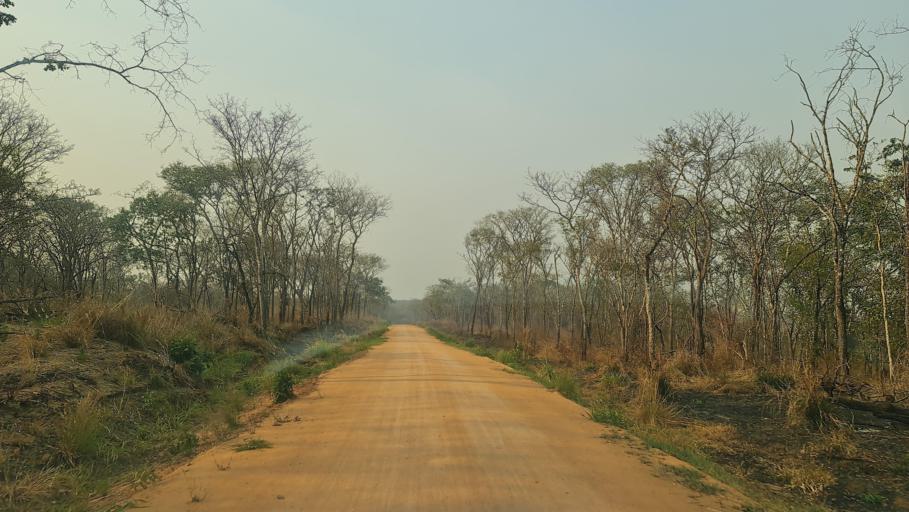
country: MZ
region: Zambezia
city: Quelimane
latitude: -17.1465
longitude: 37.1354
